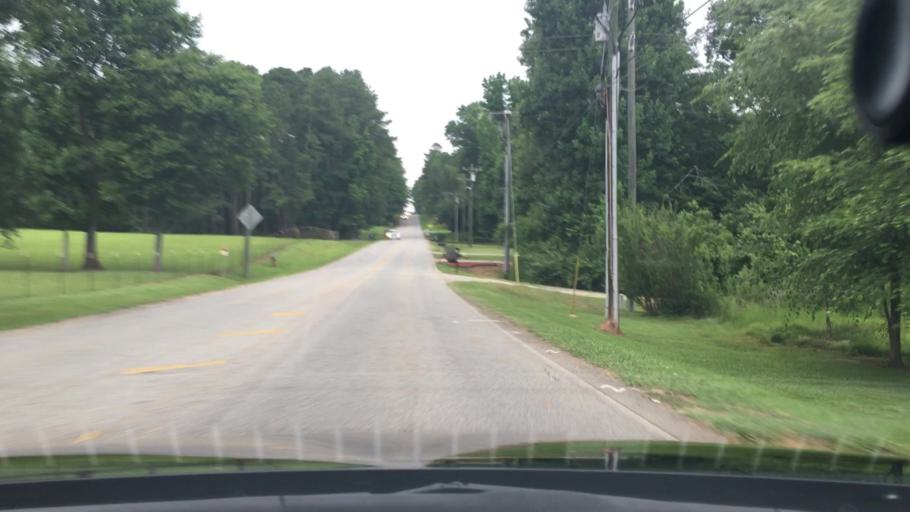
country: US
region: Georgia
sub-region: Coweta County
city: East Newnan
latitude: 33.3565
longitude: -84.7124
